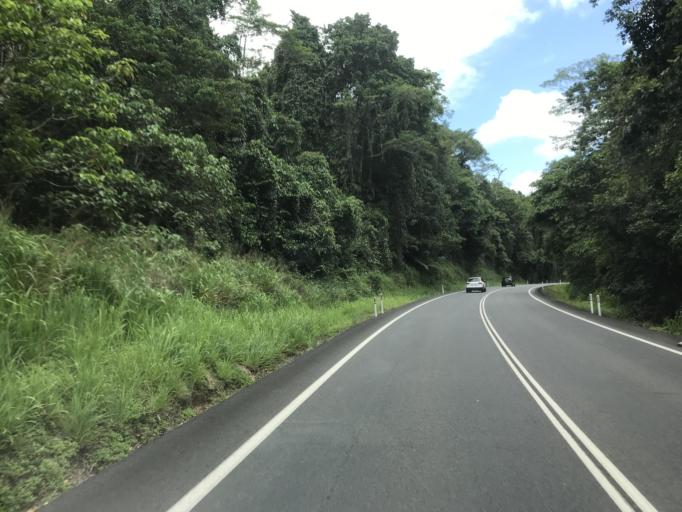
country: AU
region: Queensland
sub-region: Cassowary Coast
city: Innisfail
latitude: -17.6077
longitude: 145.7759
